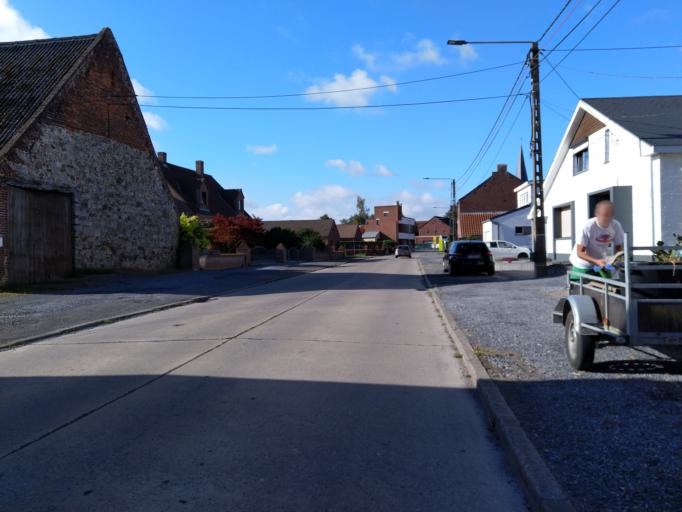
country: BE
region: Wallonia
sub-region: Province du Hainaut
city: Estinnes-au-Val
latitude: 50.4137
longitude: 4.1056
